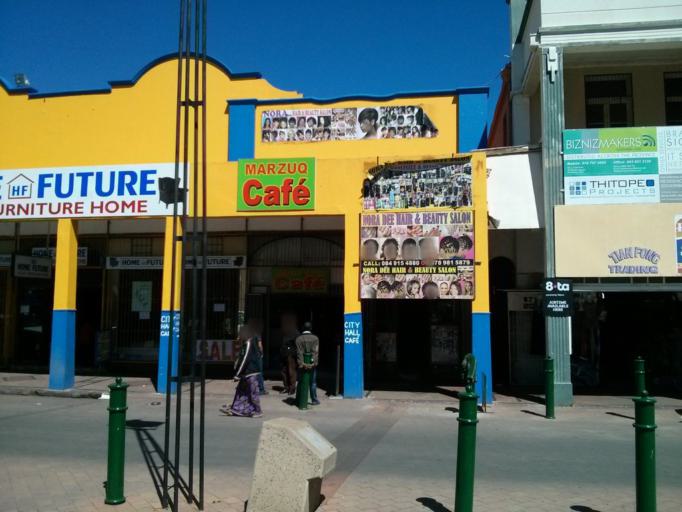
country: ZA
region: Northern Cape
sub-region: Frances Baard District Municipality
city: Kimberley
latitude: -28.7384
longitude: 24.7635
